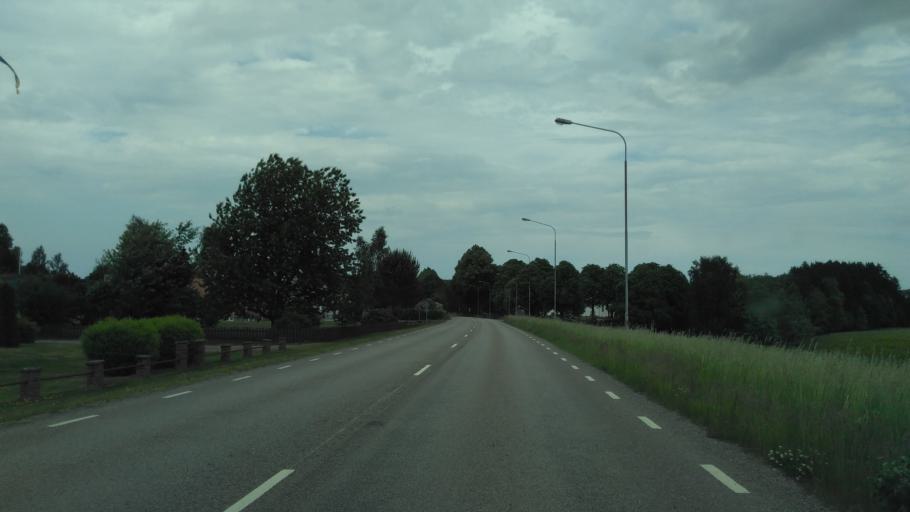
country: SE
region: Vaestra Goetaland
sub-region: Lidkopings Kommun
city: Lidkoping
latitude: 58.4367
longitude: 13.1616
